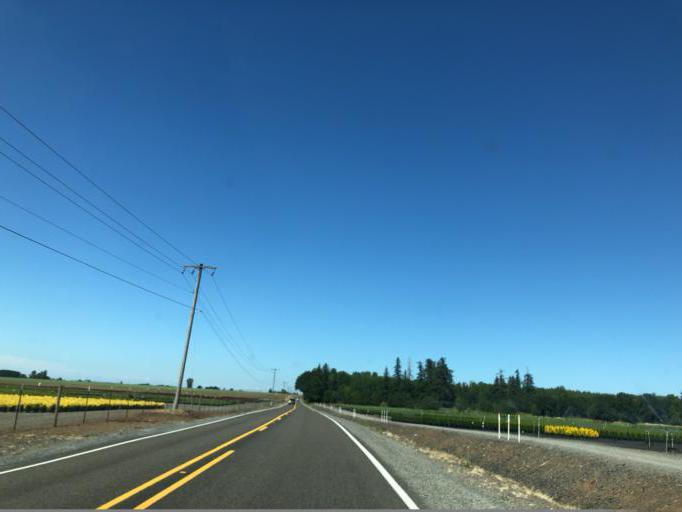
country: US
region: Oregon
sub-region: Marion County
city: Silverton
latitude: 45.0369
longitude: -122.7556
